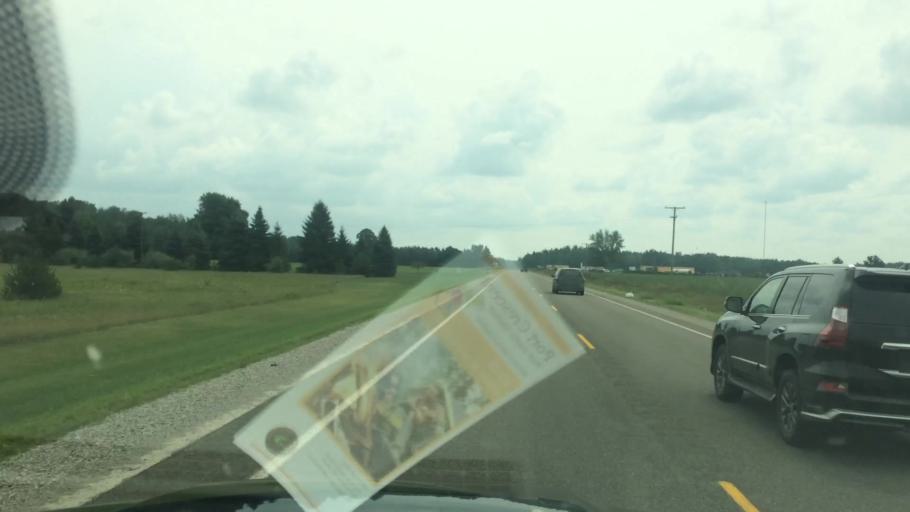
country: US
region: Michigan
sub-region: Tuscola County
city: Cass City
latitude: 43.6696
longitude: -83.0983
